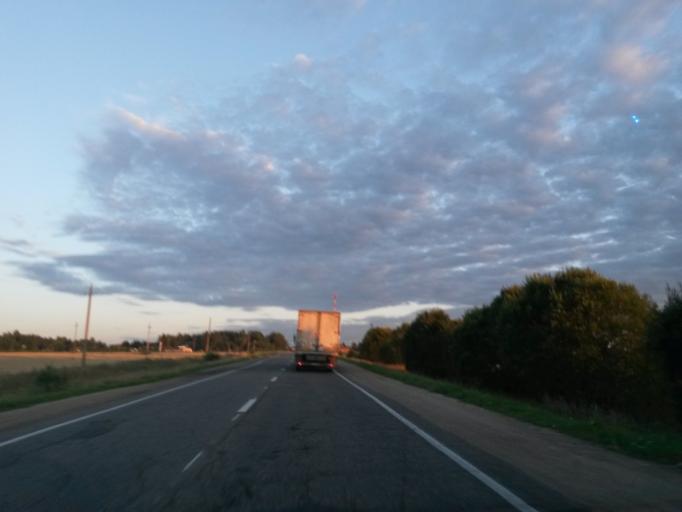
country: RU
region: Jaroslavl
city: Gavrilov-Yam
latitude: 57.3128
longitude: 39.9351
